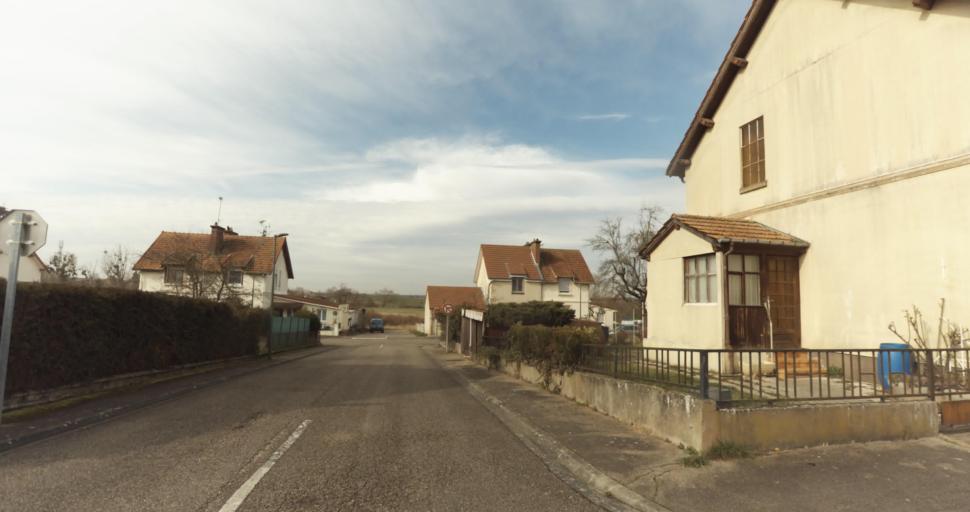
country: FR
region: Lorraine
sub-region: Departement de Meurthe-et-Moselle
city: Jarny
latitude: 49.1448
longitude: 5.8803
